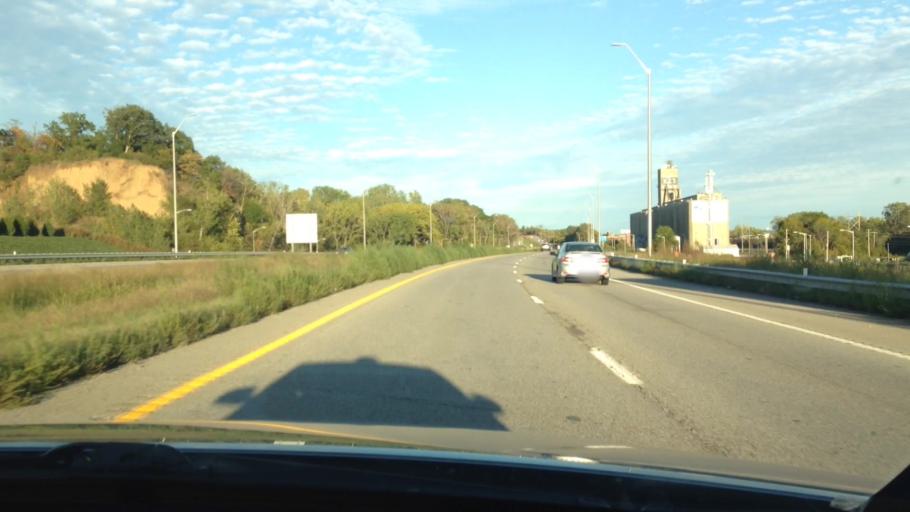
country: US
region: Missouri
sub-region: Clay County
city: North Kansas City
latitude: 39.1537
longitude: -94.5200
